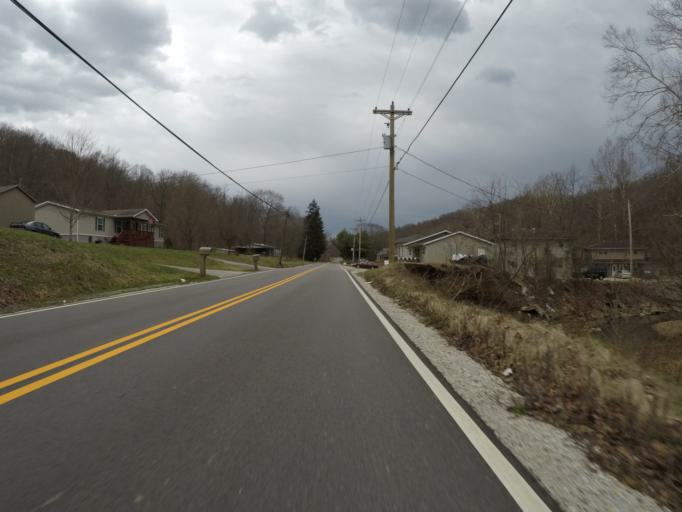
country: US
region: Ohio
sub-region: Lawrence County
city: Burlington
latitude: 38.4415
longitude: -82.5008
